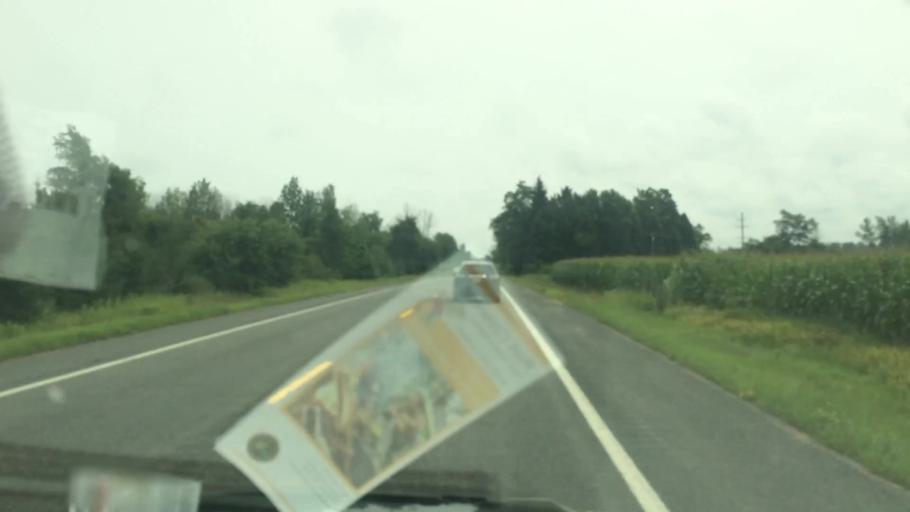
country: US
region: Michigan
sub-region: Huron County
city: Harbor Beach
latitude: 44.0153
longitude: -82.7997
